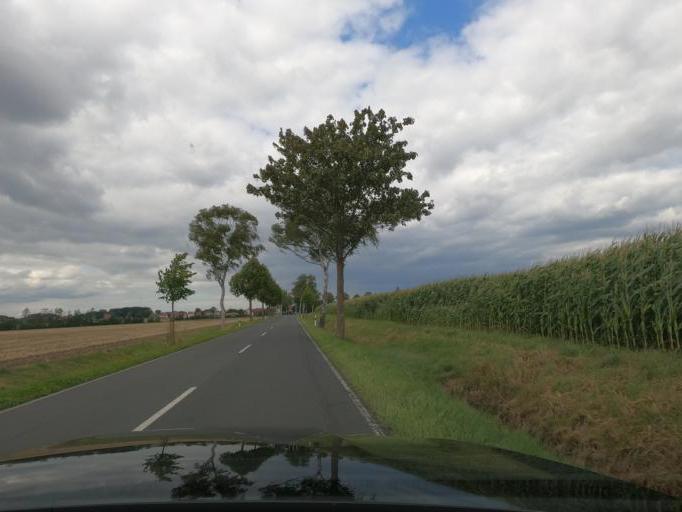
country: DE
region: Lower Saxony
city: Sehnde
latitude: 52.2890
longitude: 9.9464
